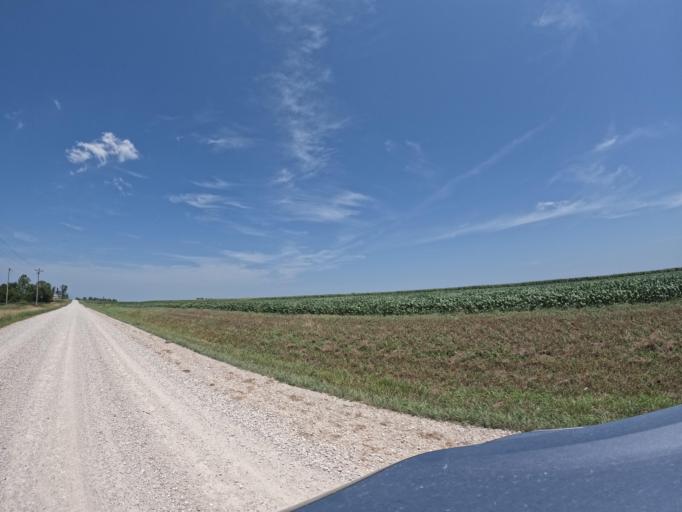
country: US
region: Iowa
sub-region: Henry County
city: Mount Pleasant
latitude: 40.9311
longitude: -91.6466
